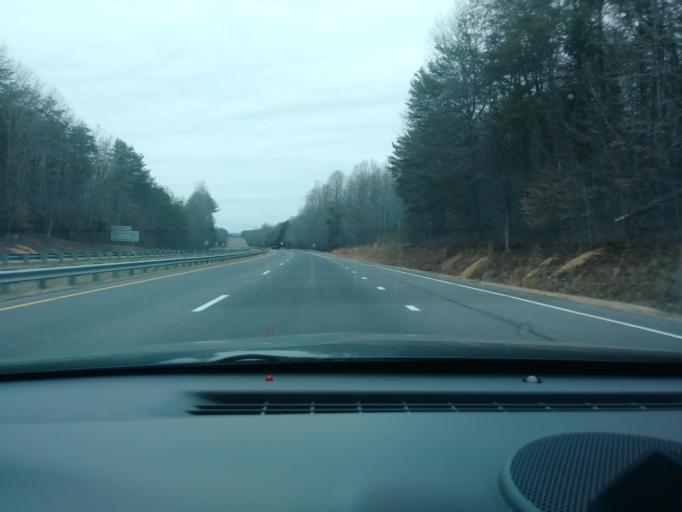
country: US
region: North Carolina
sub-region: Forsyth County
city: Lewisville
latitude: 36.1017
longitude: -80.4728
